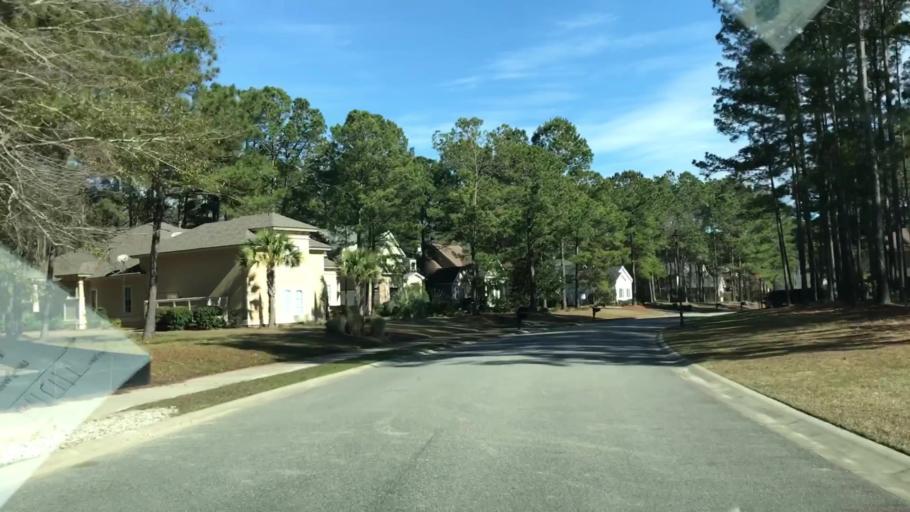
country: US
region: South Carolina
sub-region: Beaufort County
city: Bluffton
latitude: 32.2528
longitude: -80.9263
